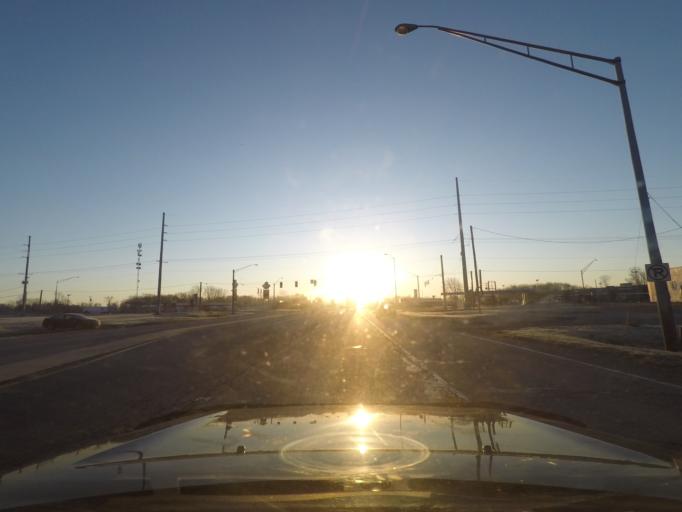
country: US
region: Indiana
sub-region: Marshall County
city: Plymouth
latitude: 41.4496
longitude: -86.3114
